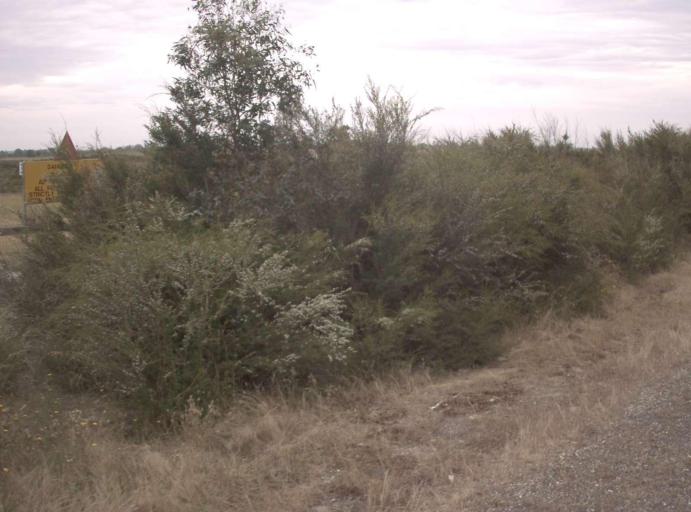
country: AU
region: Victoria
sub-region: Wellington
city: Sale
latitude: -38.1922
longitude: 147.2853
